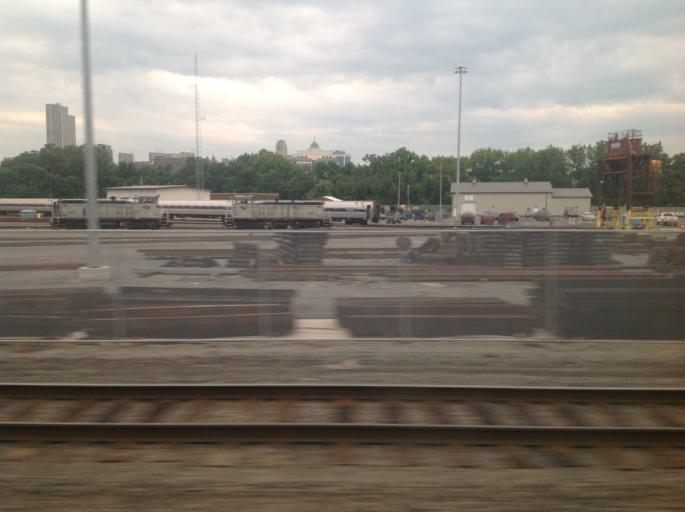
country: US
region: New York
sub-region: Rensselaer County
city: Rensselaer
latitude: 42.6503
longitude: -73.7386
